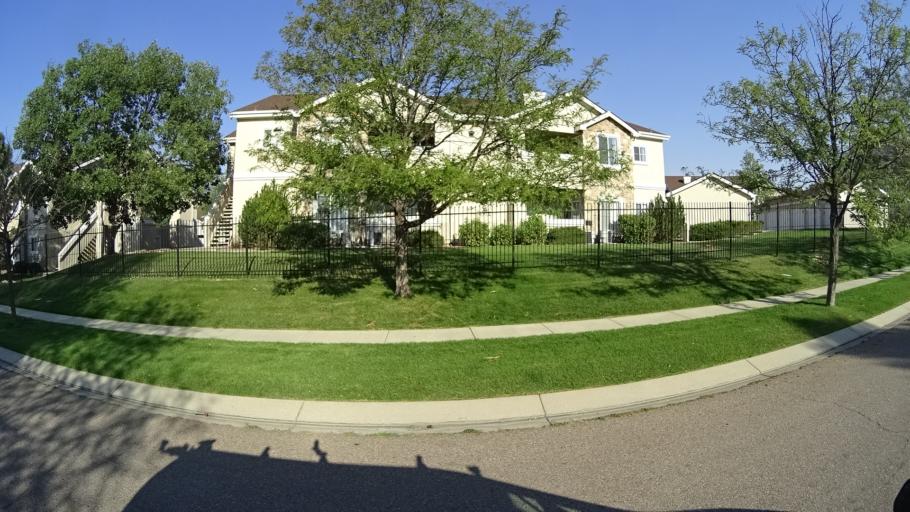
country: US
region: Colorado
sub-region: El Paso County
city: Stratmoor
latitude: 38.7773
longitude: -104.8059
